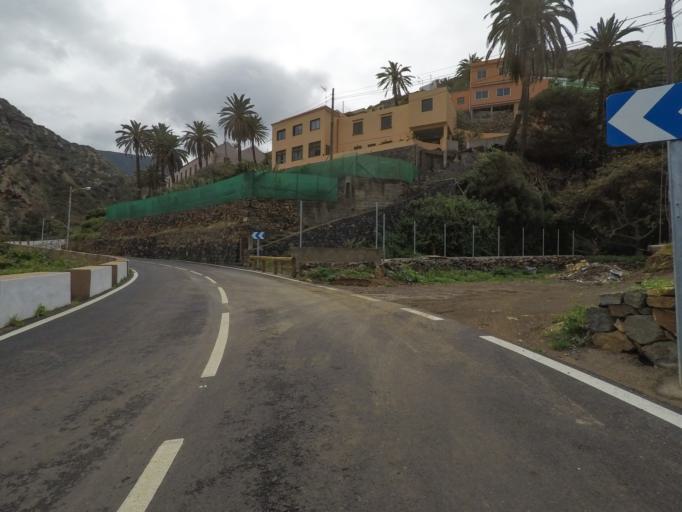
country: ES
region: Canary Islands
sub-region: Provincia de Santa Cruz de Tenerife
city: Vallehermosa
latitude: 28.1844
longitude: -17.2649
